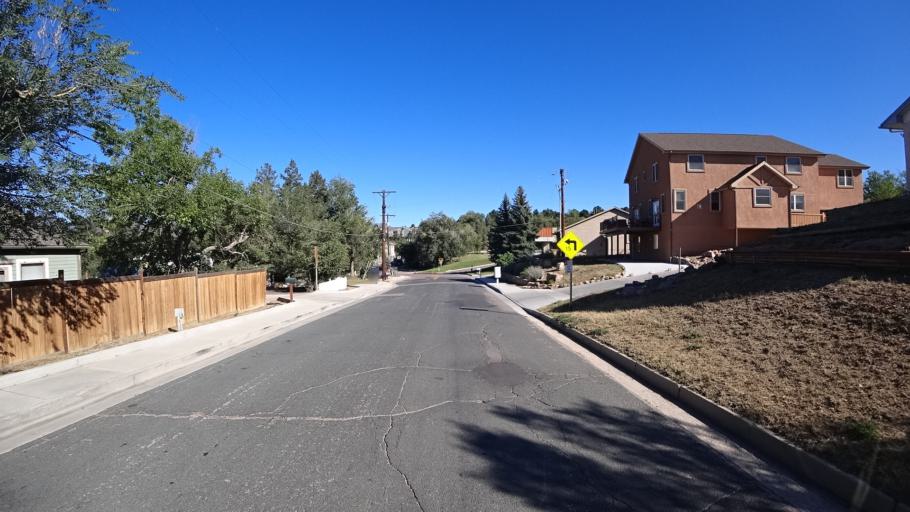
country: US
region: Colorado
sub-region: El Paso County
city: Colorado Springs
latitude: 38.8463
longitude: -104.8444
